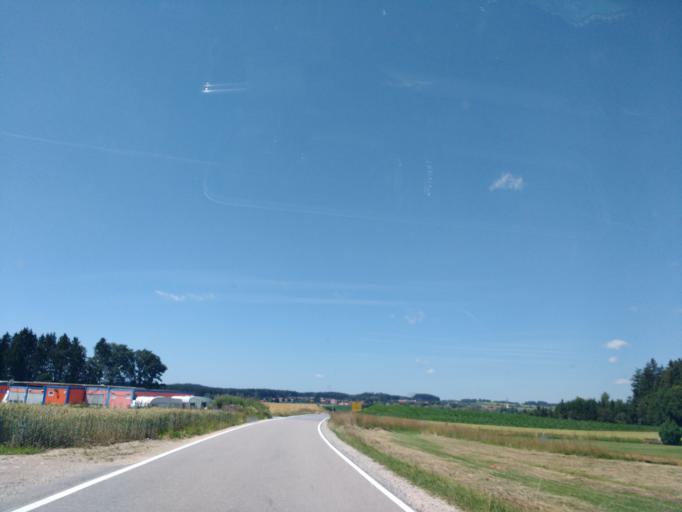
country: DE
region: Bavaria
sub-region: Upper Bavaria
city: Obing
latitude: 48.0049
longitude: 12.4339
